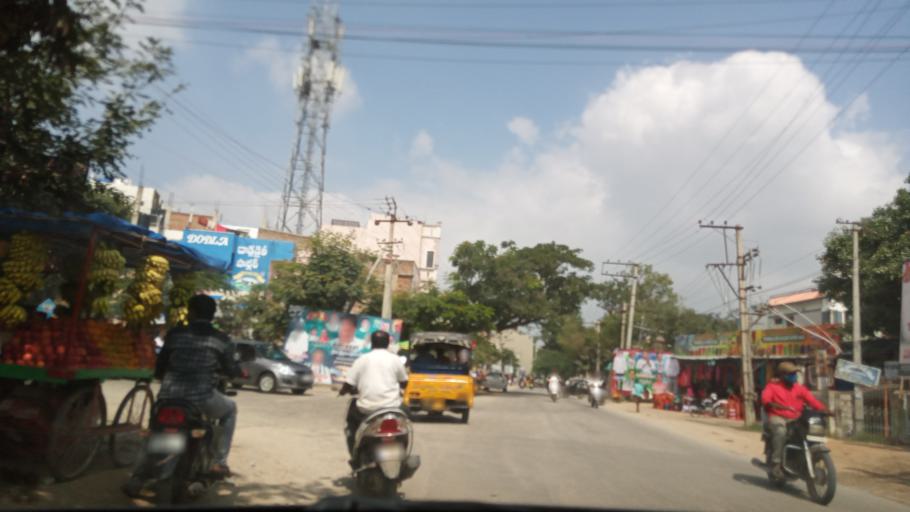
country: IN
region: Andhra Pradesh
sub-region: Chittoor
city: Madanapalle
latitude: 13.5600
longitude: 78.5098
